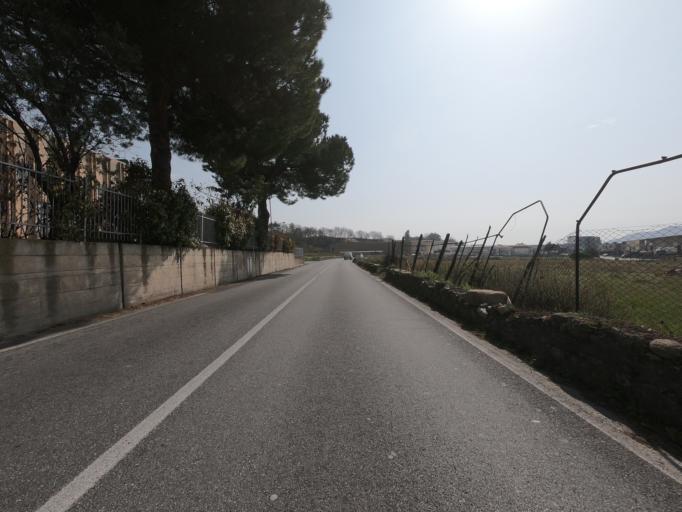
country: IT
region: Liguria
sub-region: Provincia di Savona
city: Cisano
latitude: 44.0738
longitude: 8.1642
